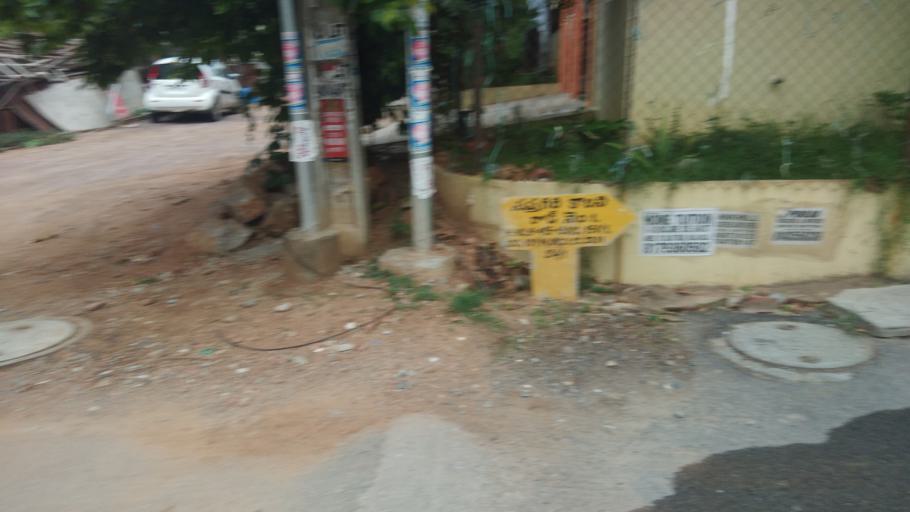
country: IN
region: Telangana
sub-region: Medak
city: Serilingampalle
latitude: 17.4891
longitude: 78.3508
